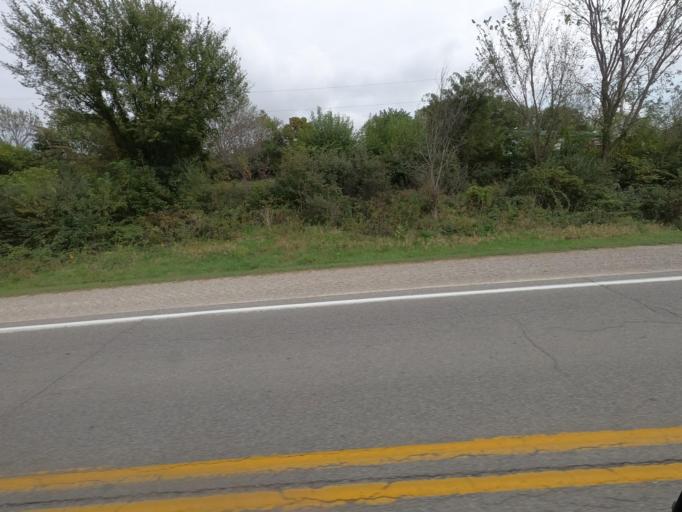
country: US
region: Iowa
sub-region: Wapello County
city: Ottumwa
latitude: 40.9279
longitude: -92.2279
